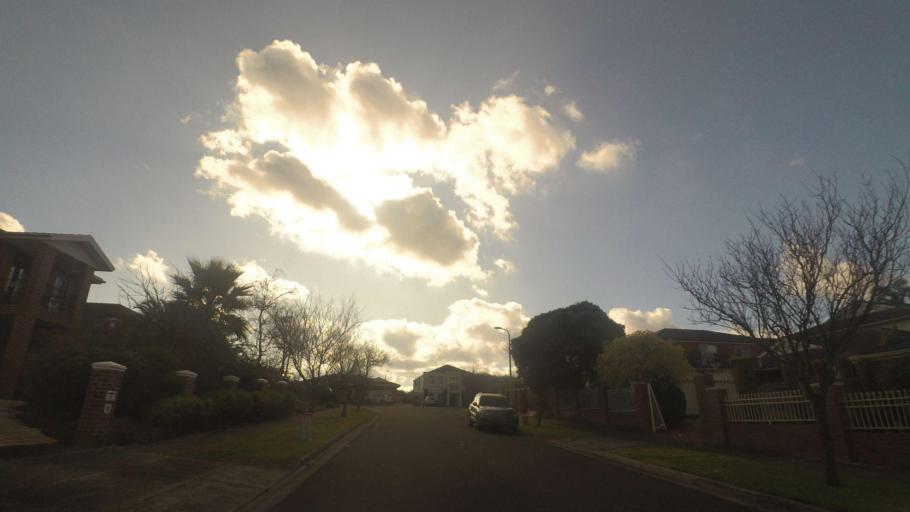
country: AU
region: Victoria
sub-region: Knox
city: Rowville
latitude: -37.9250
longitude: 145.2407
